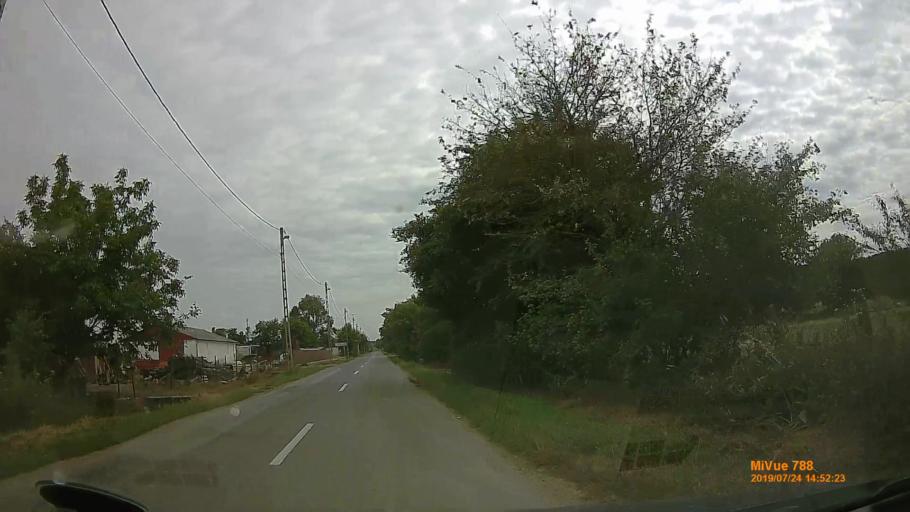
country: HU
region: Szabolcs-Szatmar-Bereg
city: Aranyosapati
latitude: 48.2632
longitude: 22.2886
